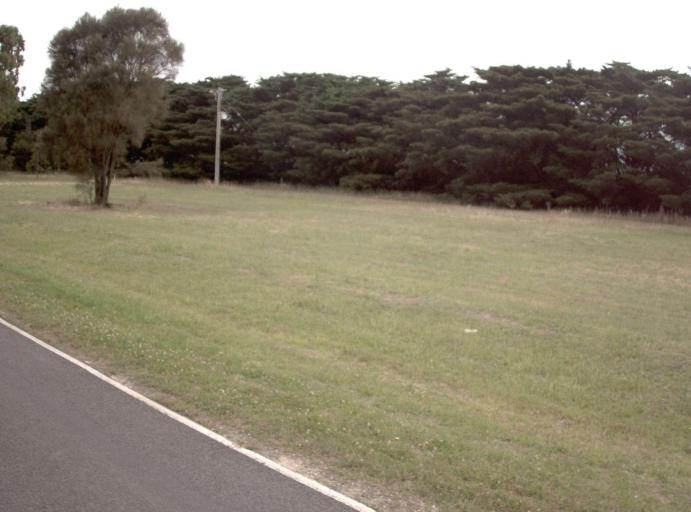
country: AU
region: Victoria
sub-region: Wellington
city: Heyfield
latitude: -38.0589
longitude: 146.7690
